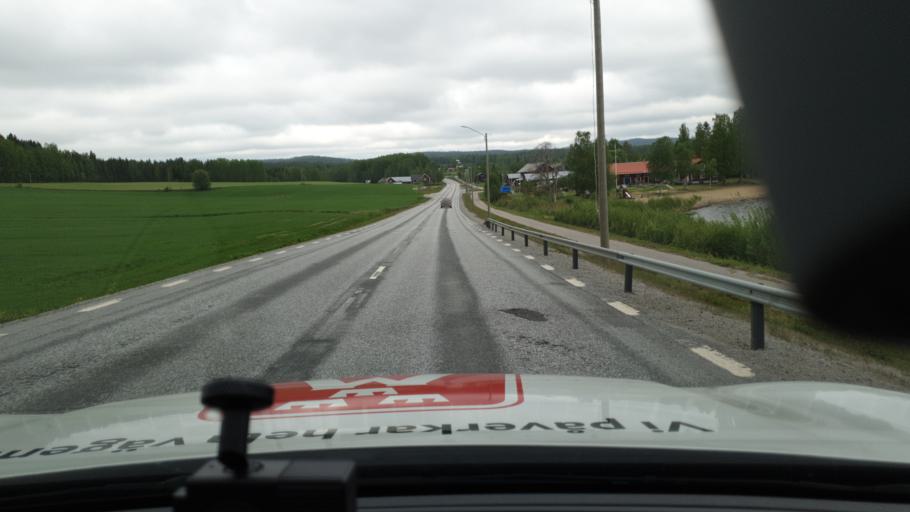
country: SE
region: Vaesterbotten
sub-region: Vannas Kommun
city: Vannasby
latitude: 64.0215
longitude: 20.0255
